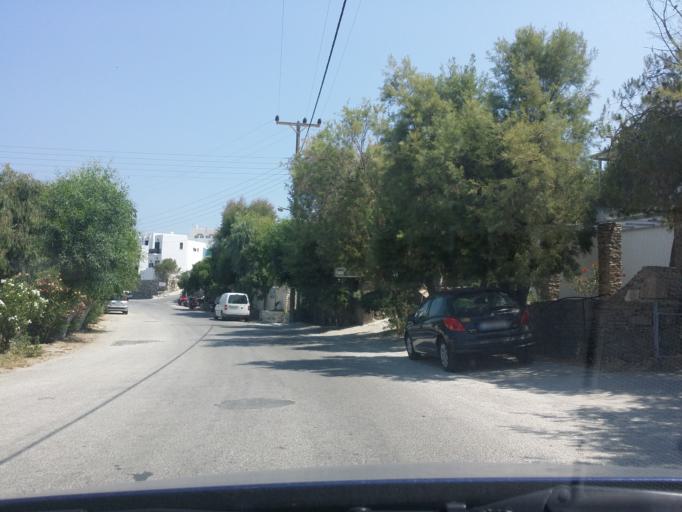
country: GR
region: South Aegean
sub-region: Nomos Kykladon
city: Naousa
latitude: 37.1203
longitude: 25.2330
